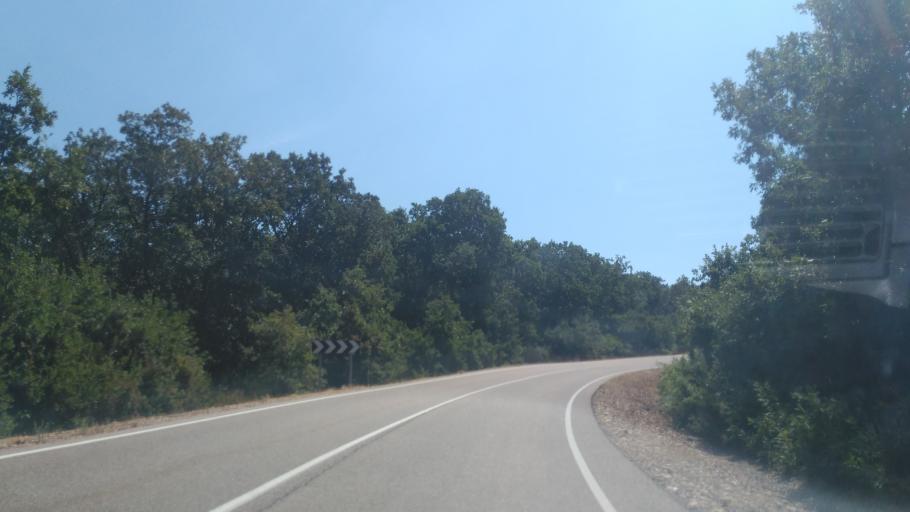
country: ES
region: Castille and Leon
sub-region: Provincia de Salamanca
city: Cilleros de la Bastida
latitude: 40.5587
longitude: -6.0719
